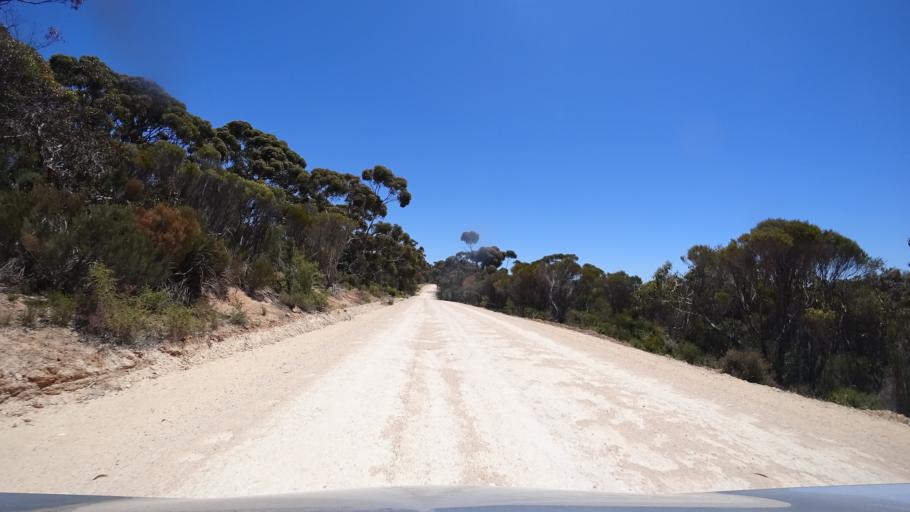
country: AU
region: South Australia
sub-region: Kangaroo Island
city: Kingscote
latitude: -35.6510
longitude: 137.1701
